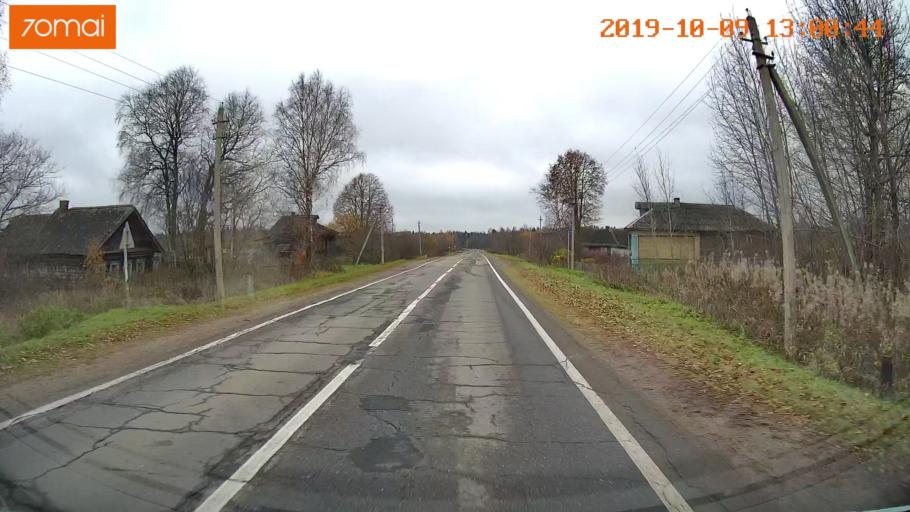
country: RU
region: Jaroslavl
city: Prechistoye
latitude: 58.3744
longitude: 40.4826
